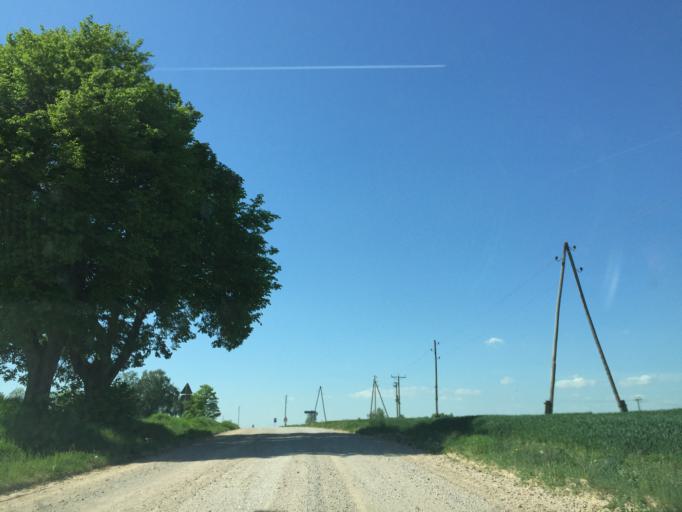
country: LV
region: Rundales
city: Pilsrundale
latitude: 56.4917
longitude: 24.0767
